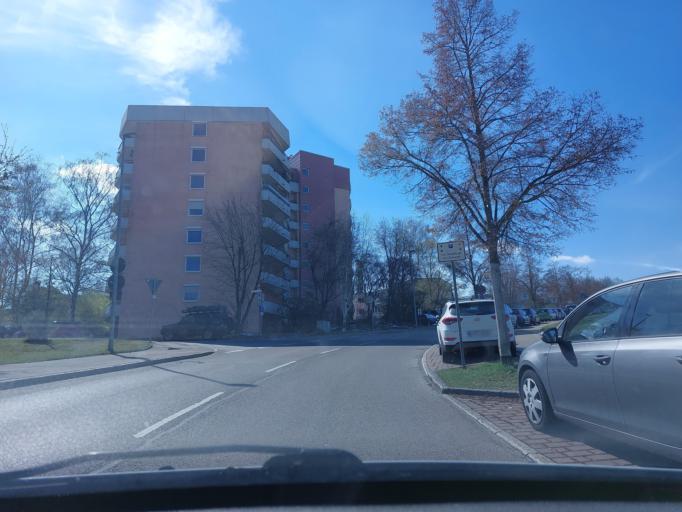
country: DE
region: Baden-Wuerttemberg
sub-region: Regierungsbezirk Stuttgart
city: Filderstadt
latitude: 48.6497
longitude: 9.2047
